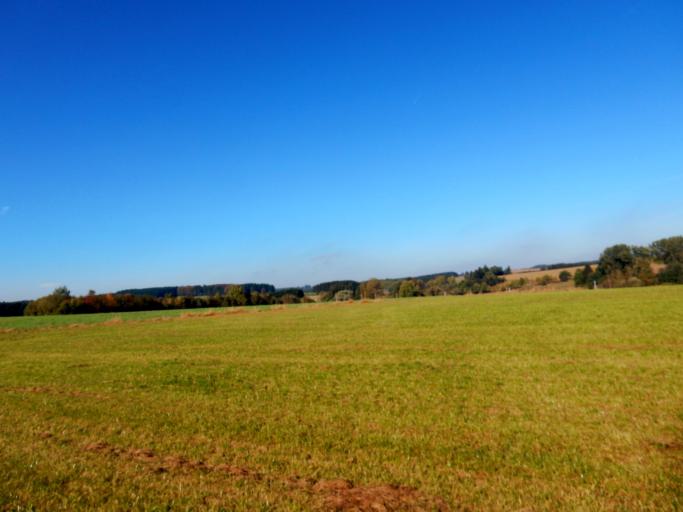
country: LU
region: Diekirch
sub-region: Canton de Clervaux
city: Troisvierges
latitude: 50.1315
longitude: 5.9808
